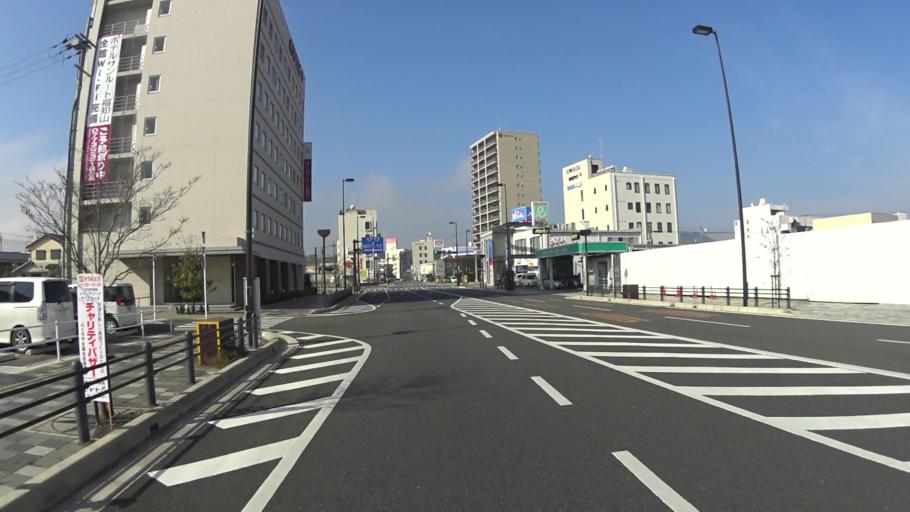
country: JP
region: Kyoto
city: Fukuchiyama
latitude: 35.2979
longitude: 135.1170
